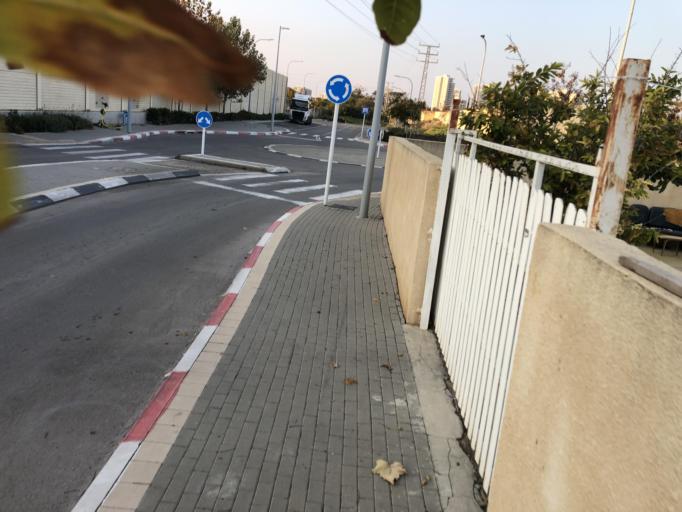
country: IL
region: Northern District
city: `Akko
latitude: 32.9281
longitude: 35.0835
